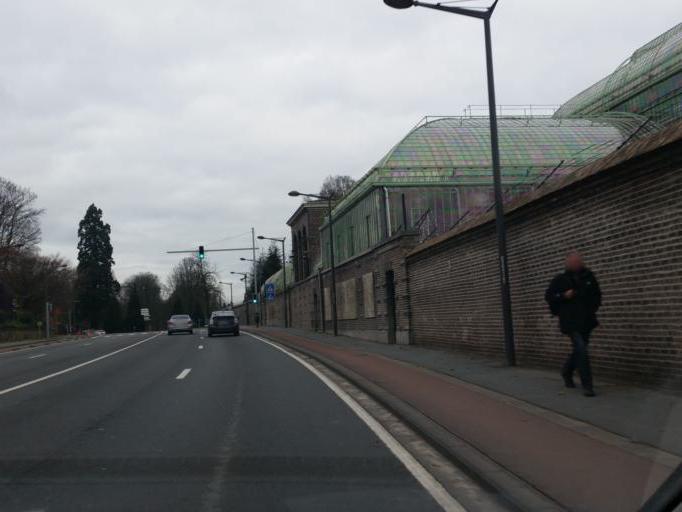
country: BE
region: Brussels Capital
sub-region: Bruxelles-Capitale
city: Brussels
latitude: 50.8915
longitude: 4.3585
